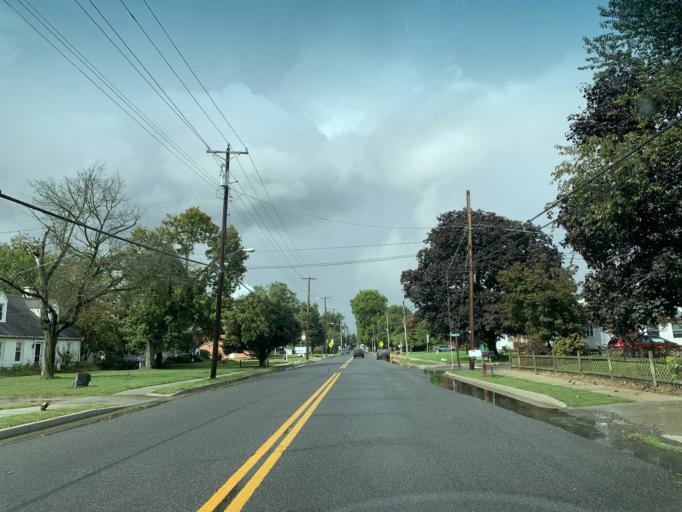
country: US
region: Maryland
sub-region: Queen Anne's County
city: Kingstown
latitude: 39.1826
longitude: -75.8580
